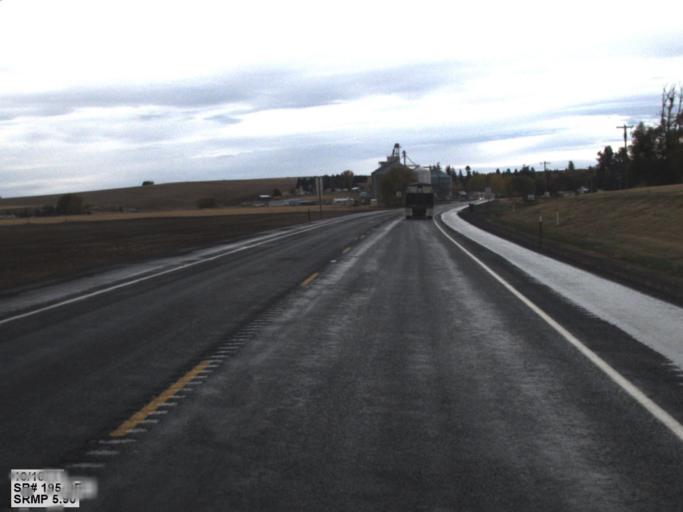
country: US
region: Washington
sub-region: Asotin County
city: Clarkston
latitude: 46.5476
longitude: -117.0950
